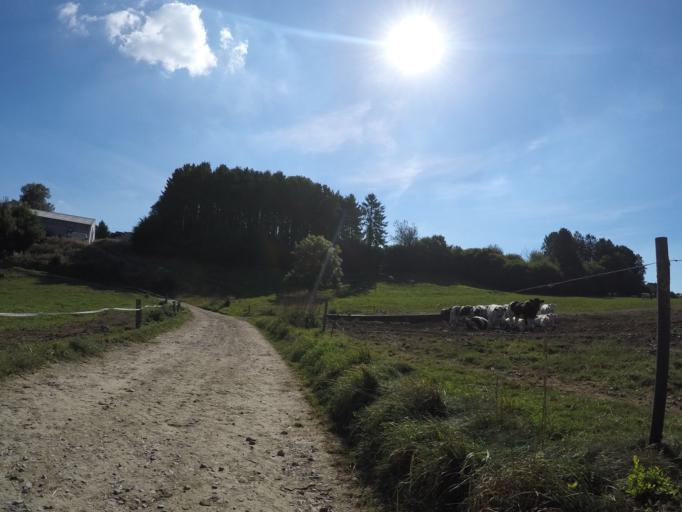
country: BE
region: Wallonia
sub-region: Province de Namur
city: Ciney
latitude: 50.3139
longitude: 5.0583
